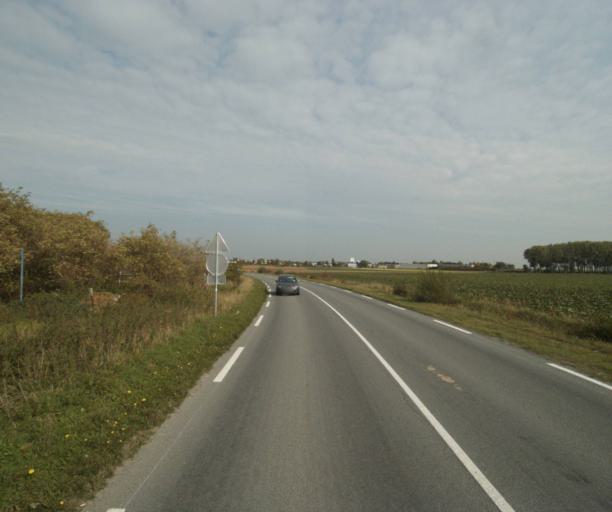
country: FR
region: Nord-Pas-de-Calais
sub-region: Departement du Nord
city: Templemars
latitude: 50.5644
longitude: 3.0540
